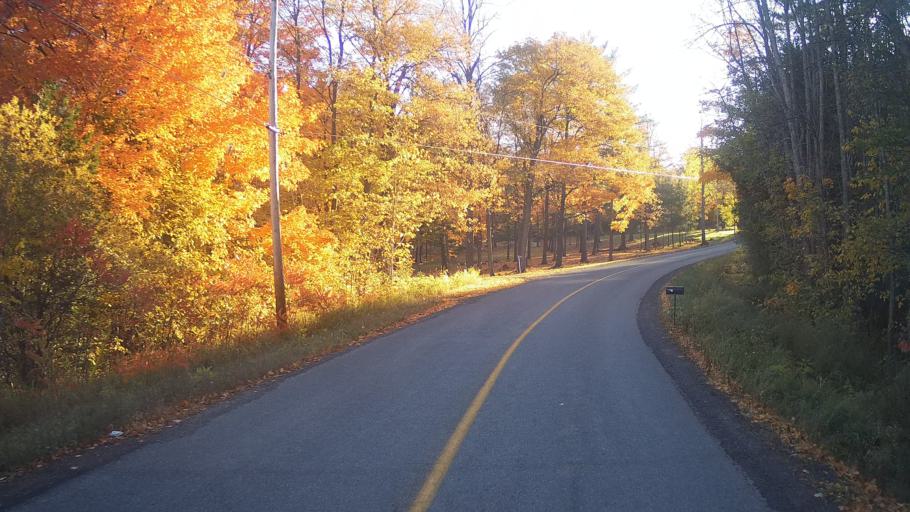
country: CA
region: Ontario
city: Arnprior
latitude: 45.3453
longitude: -76.3276
